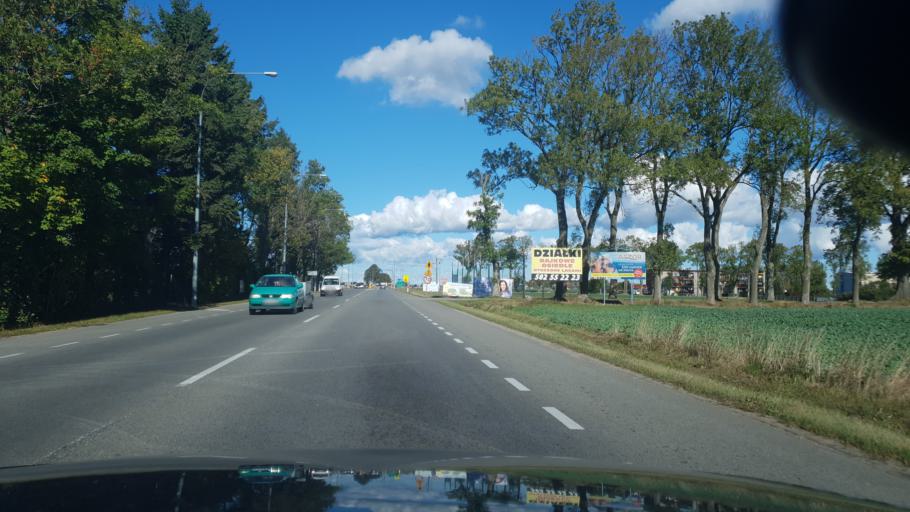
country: PL
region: Pomeranian Voivodeship
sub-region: Powiat pucki
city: Zelistrzewo
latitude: 54.6835
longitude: 18.3709
